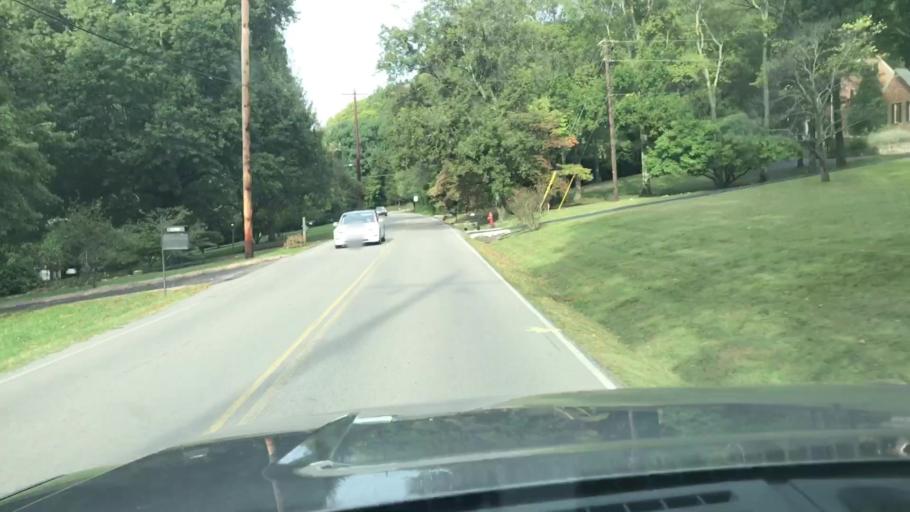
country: US
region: Tennessee
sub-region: Davidson County
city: Forest Hills
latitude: 36.0666
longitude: -86.8206
